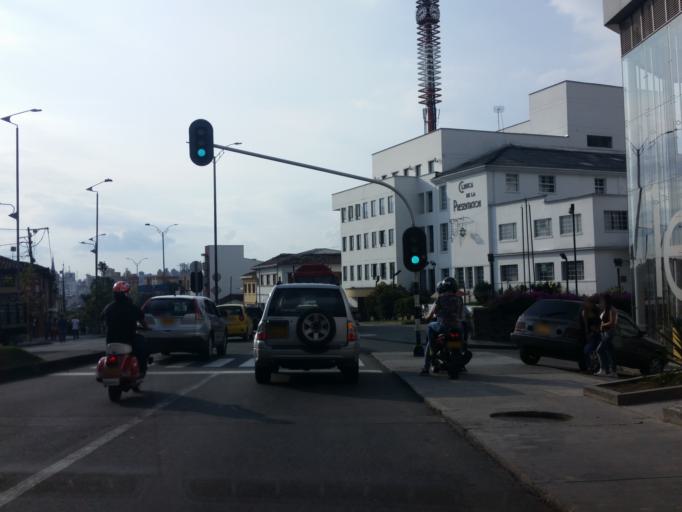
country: CO
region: Caldas
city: Manizales
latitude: 5.0654
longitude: -75.5014
